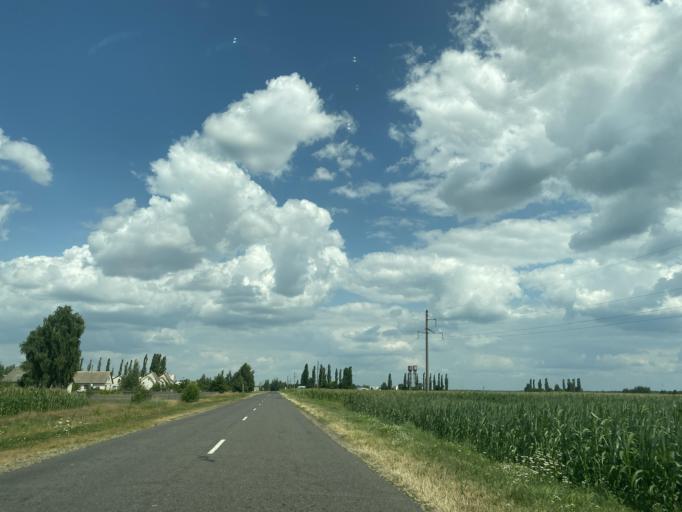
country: BY
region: Brest
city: Ivanava
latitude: 52.3422
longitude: 25.6257
